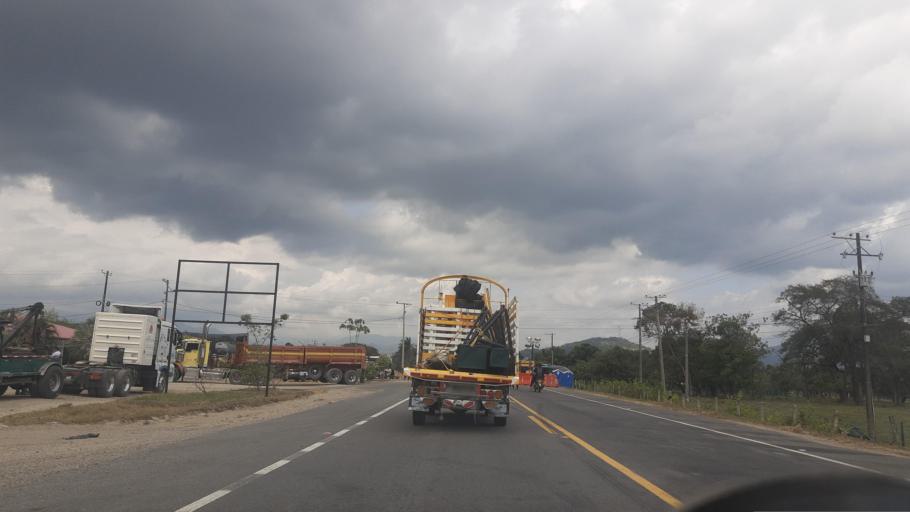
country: CO
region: Casanare
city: Tauramena
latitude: 4.9898
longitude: -72.6849
